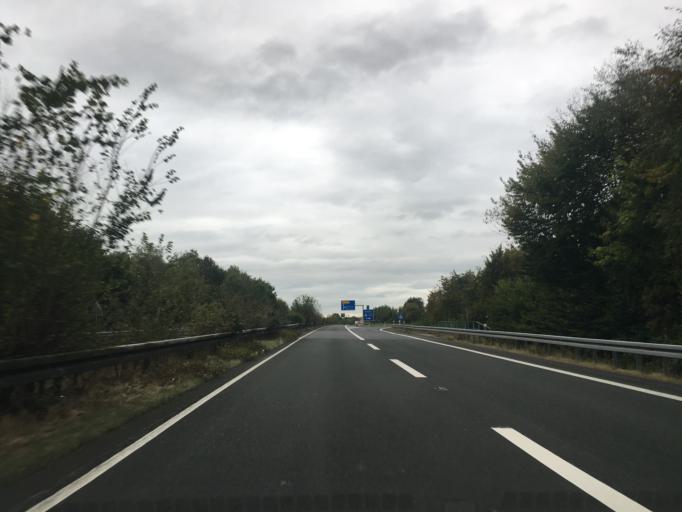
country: DE
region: North Rhine-Westphalia
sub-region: Regierungsbezirk Munster
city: Ochtrup
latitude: 52.1924
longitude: 7.1226
